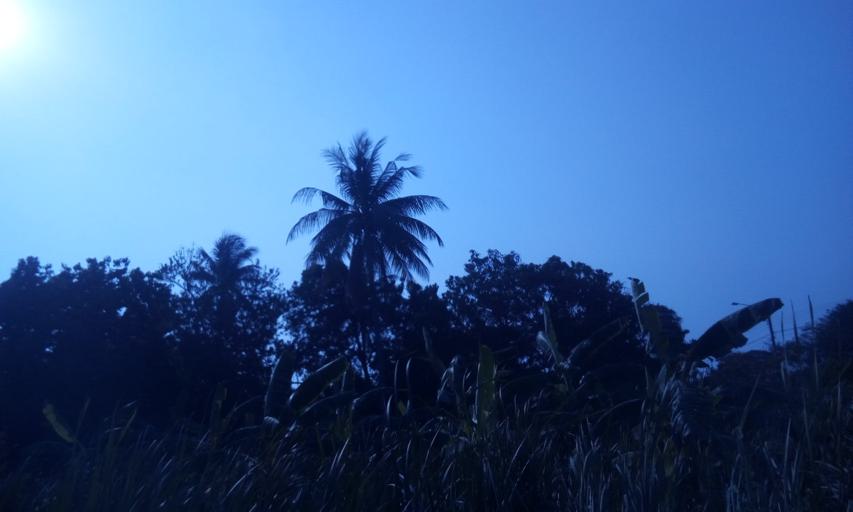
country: TH
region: Nonthaburi
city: Sai Noi
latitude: 13.9752
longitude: 100.3196
